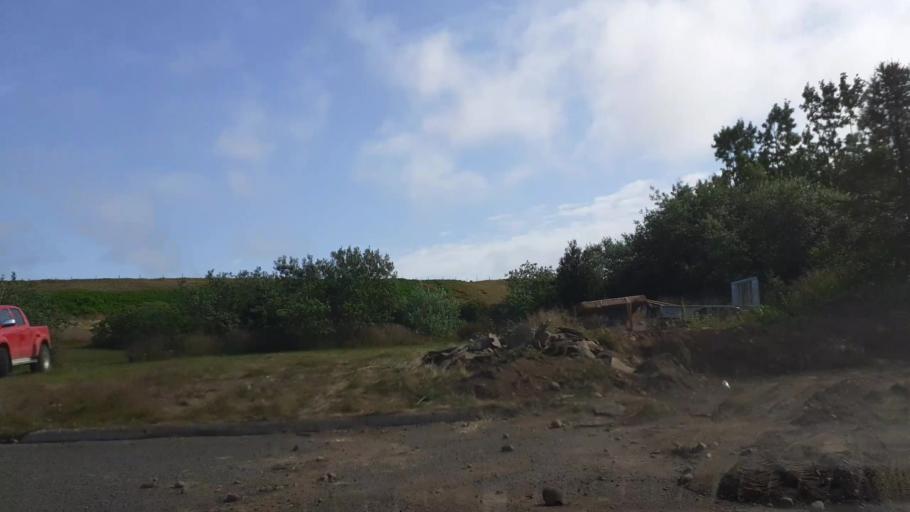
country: IS
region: Northwest
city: Saudarkrokur
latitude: 65.6623
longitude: -20.2733
